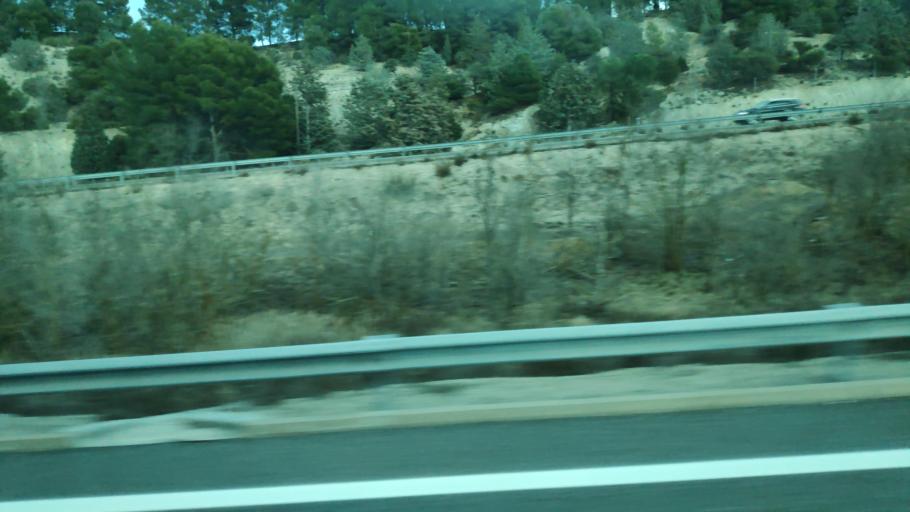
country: ES
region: Castille-La Mancha
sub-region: Provincia de Cuenca
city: Tarancon
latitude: 40.0207
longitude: -3.0343
